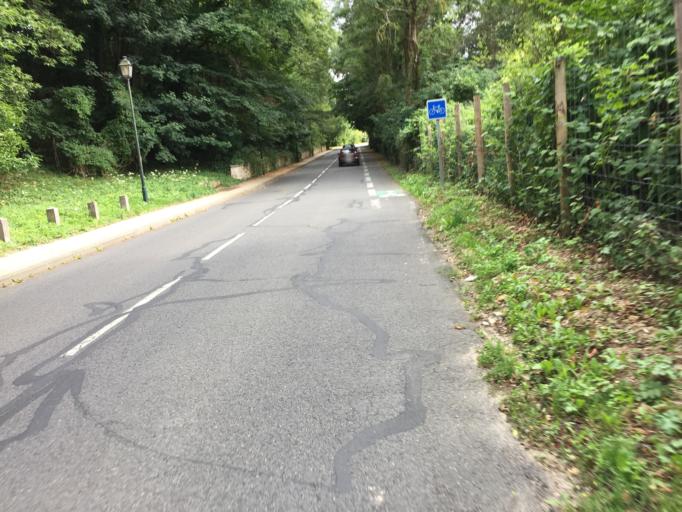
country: FR
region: Ile-de-France
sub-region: Departement des Yvelines
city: Guyancourt
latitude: 48.7775
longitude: 2.0621
